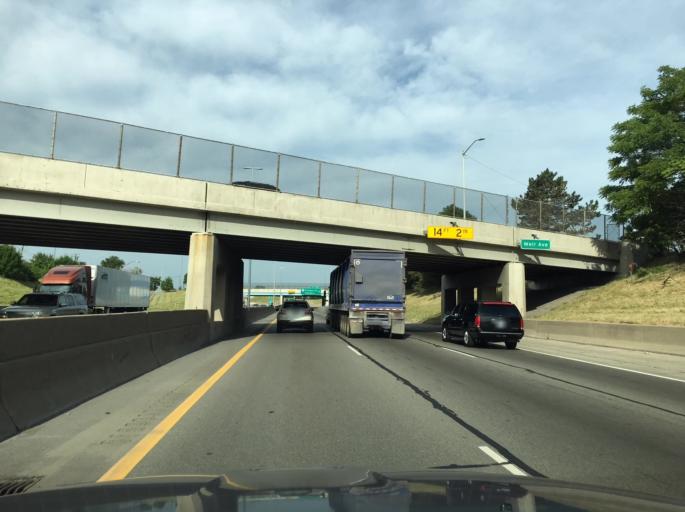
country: US
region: Michigan
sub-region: Wayne County
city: Dearborn
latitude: 42.3295
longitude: -83.1540
